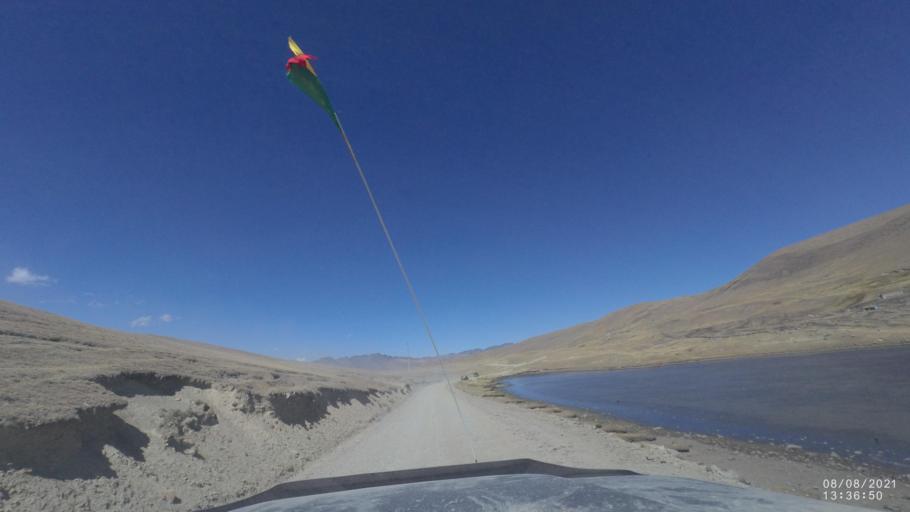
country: BO
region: Cochabamba
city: Colchani
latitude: -17.0755
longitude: -66.5001
